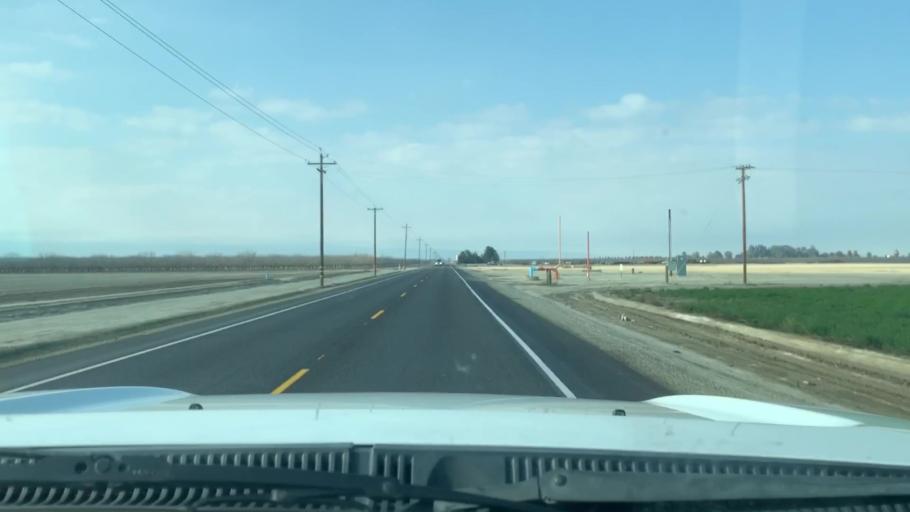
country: US
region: California
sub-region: Kern County
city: Buttonwillow
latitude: 35.4423
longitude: -119.4141
